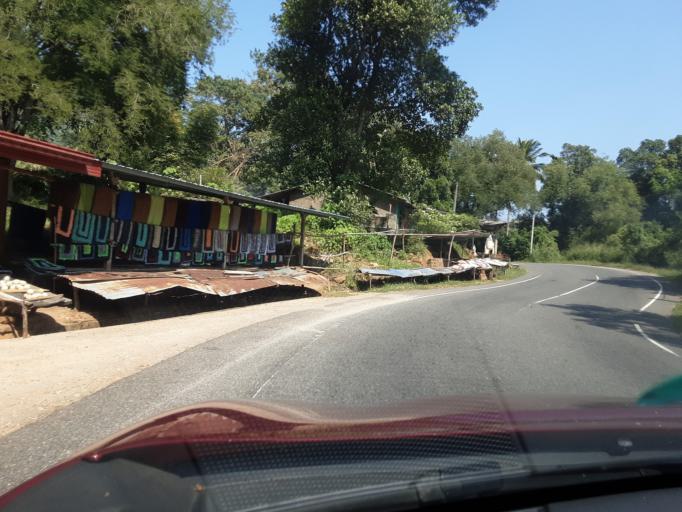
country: LK
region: Uva
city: Badulla
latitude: 7.1567
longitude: 81.0544
